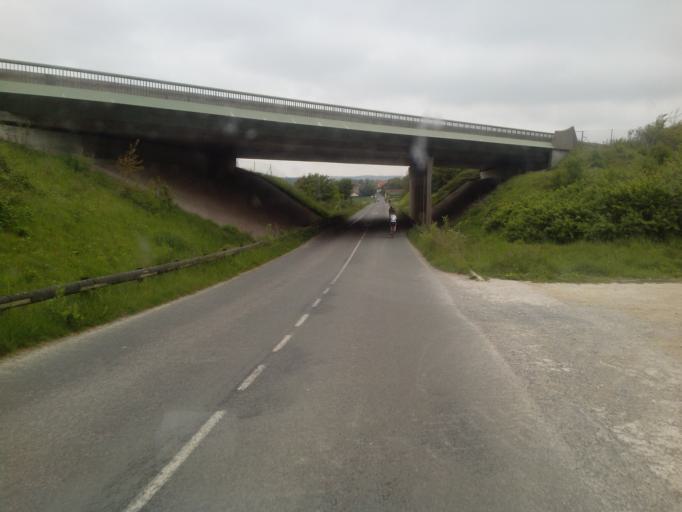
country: FR
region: Nord-Pas-de-Calais
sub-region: Departement du Pas-de-Calais
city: Nesles
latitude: 50.6141
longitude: 1.6574
